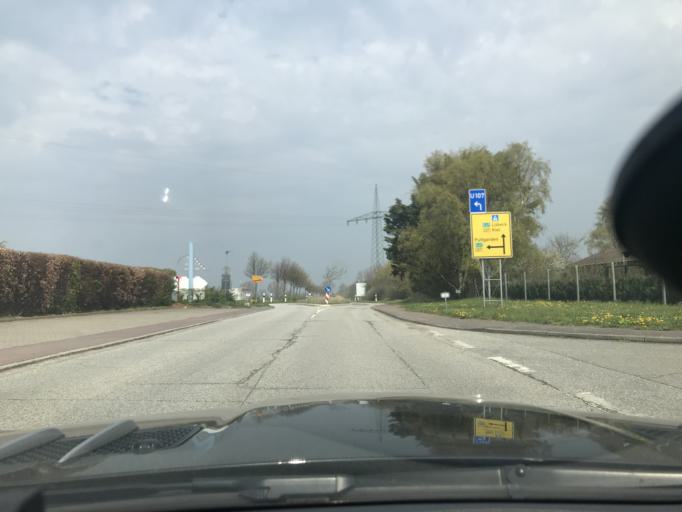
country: DE
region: Schleswig-Holstein
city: Grossenbrode
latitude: 54.3760
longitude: 11.0851
